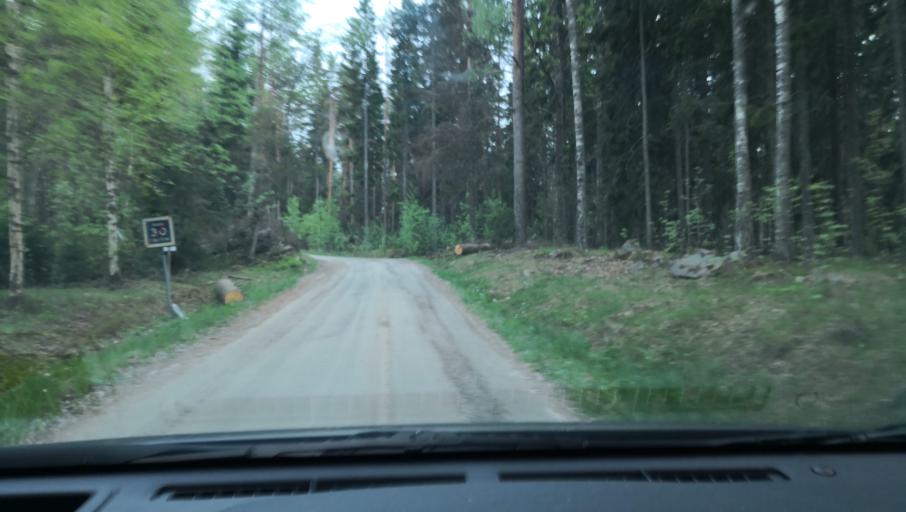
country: SE
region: Vaestmanland
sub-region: Skinnskattebergs Kommun
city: Skinnskatteberg
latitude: 59.7412
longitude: 15.4697
